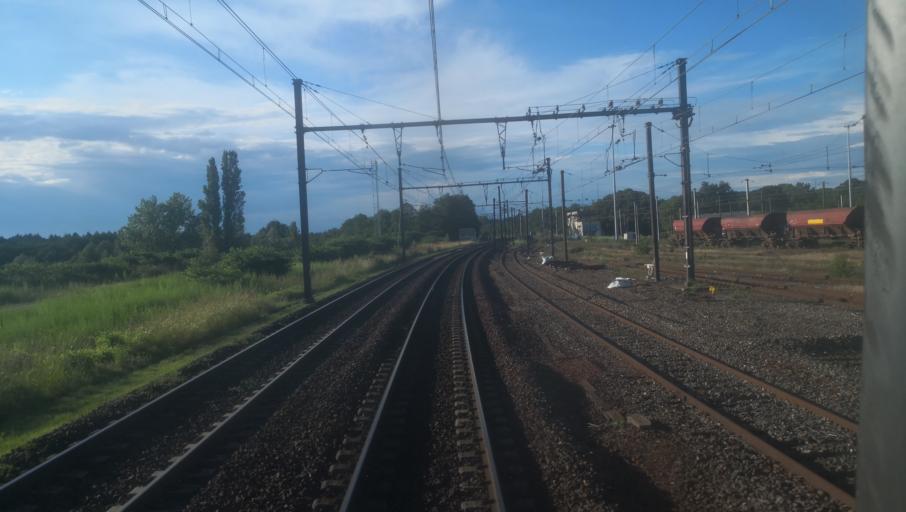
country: FR
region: Centre
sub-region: Departement du Cher
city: Vierzon
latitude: 47.2397
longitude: 2.0465
